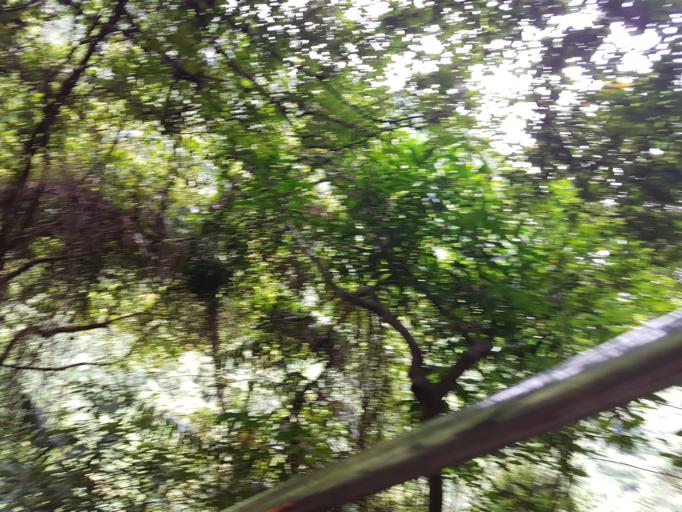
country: TW
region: Taiwan
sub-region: Keelung
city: Keelung
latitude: 25.0487
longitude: 121.6658
